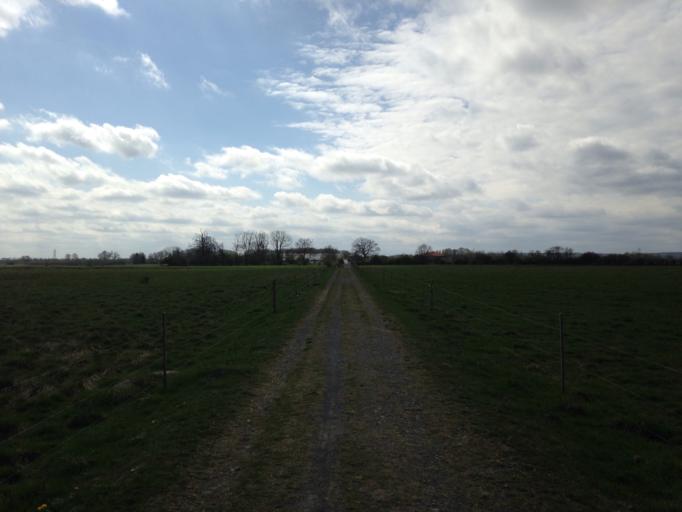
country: SE
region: Skane
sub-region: Kristianstads Kommun
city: Kristianstad
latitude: 56.0404
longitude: 14.1282
